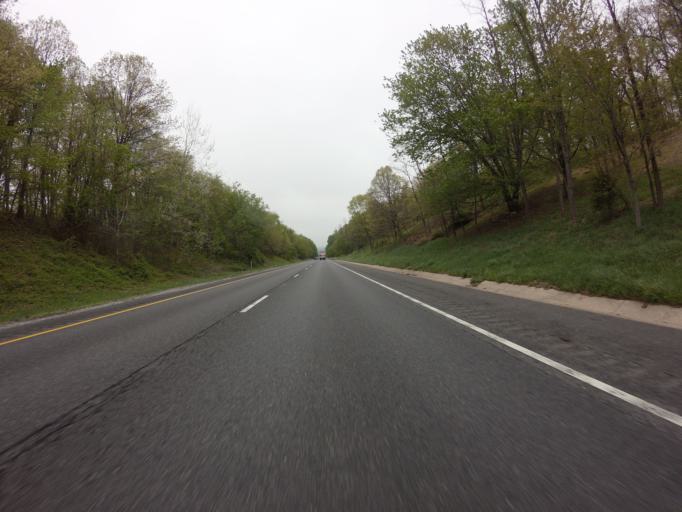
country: US
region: Maryland
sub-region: Washington County
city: Boonsboro
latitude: 39.5533
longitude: -77.6094
